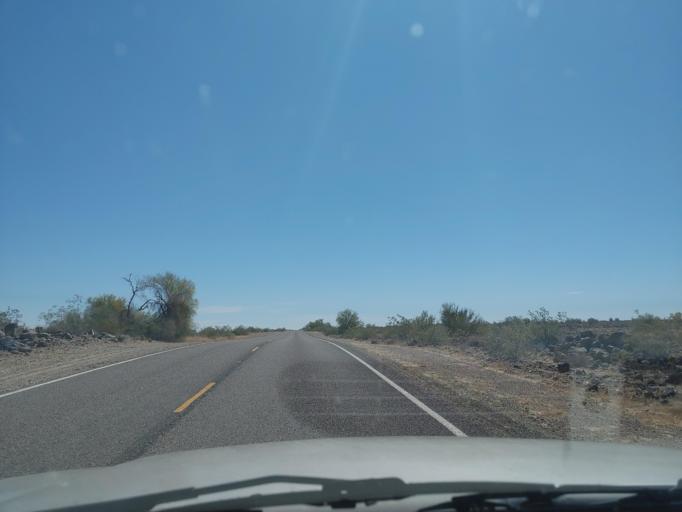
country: US
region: Arizona
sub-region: Maricopa County
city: Gila Bend
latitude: 32.9095
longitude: -113.2695
